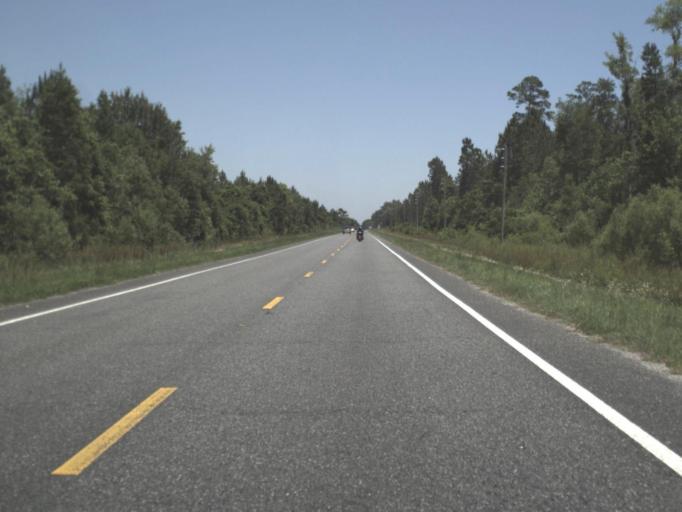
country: US
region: Florida
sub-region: Columbia County
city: Watertown
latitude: 30.2021
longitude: -82.4537
